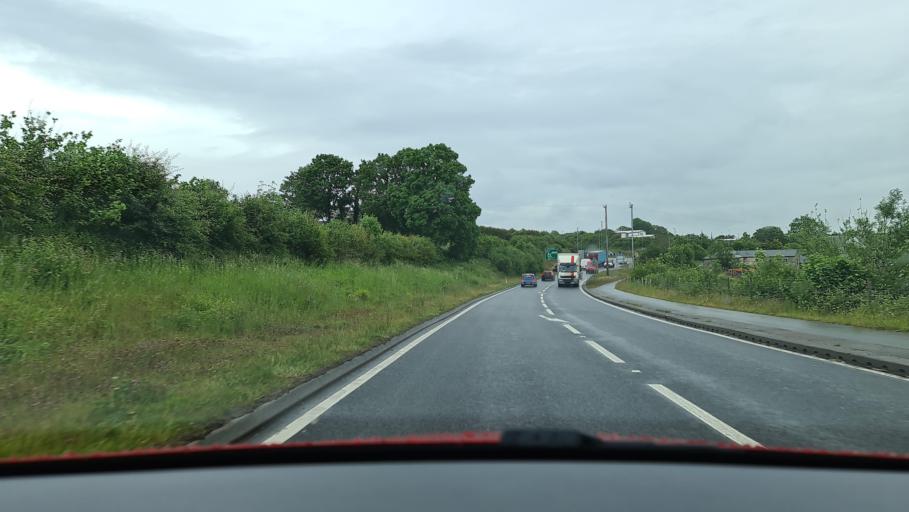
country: GB
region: England
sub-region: Cornwall
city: Liskeard
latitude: 50.4583
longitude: -4.5304
